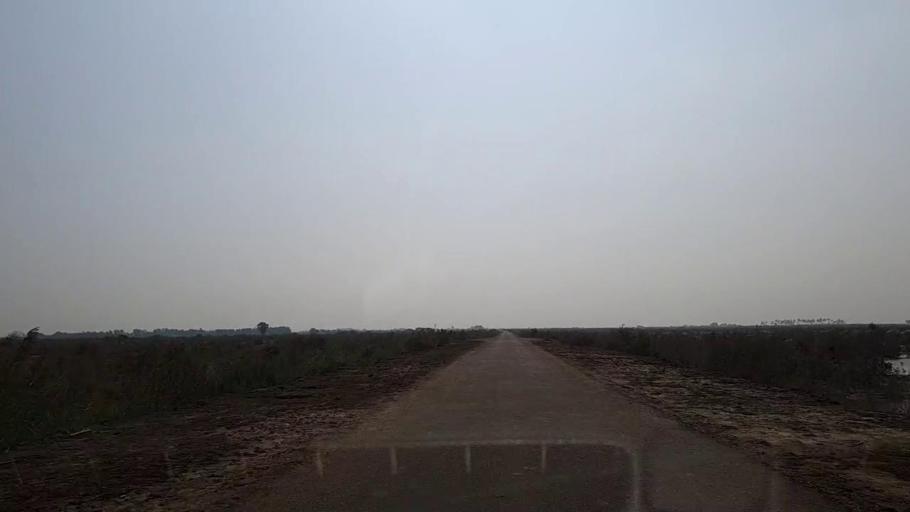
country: PK
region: Sindh
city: Gharo
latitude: 24.6647
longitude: 67.6942
